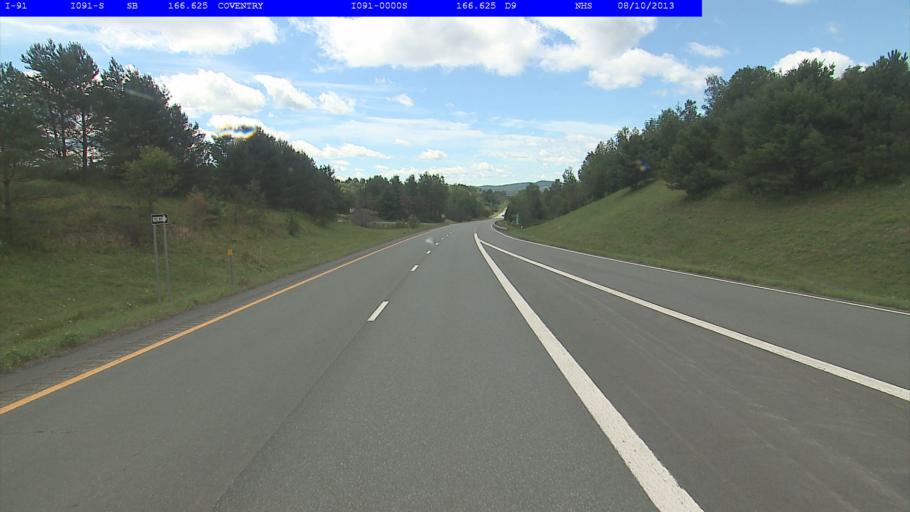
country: US
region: Vermont
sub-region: Orleans County
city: Newport
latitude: 44.8746
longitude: -72.1757
